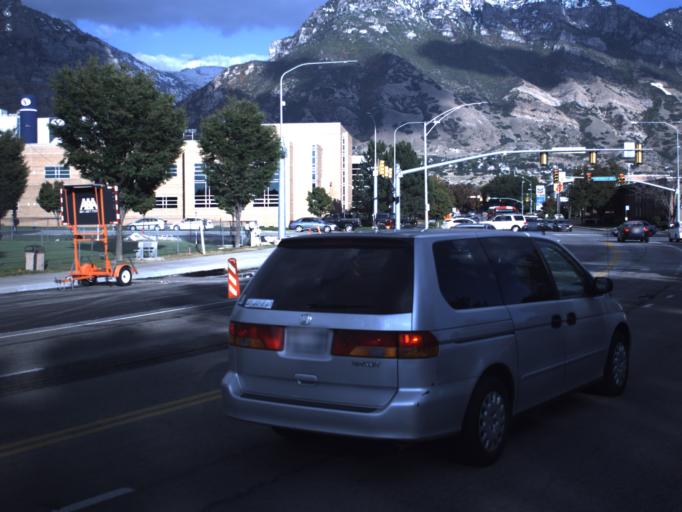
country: US
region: Utah
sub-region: Utah County
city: Provo
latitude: 40.2560
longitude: -111.6597
